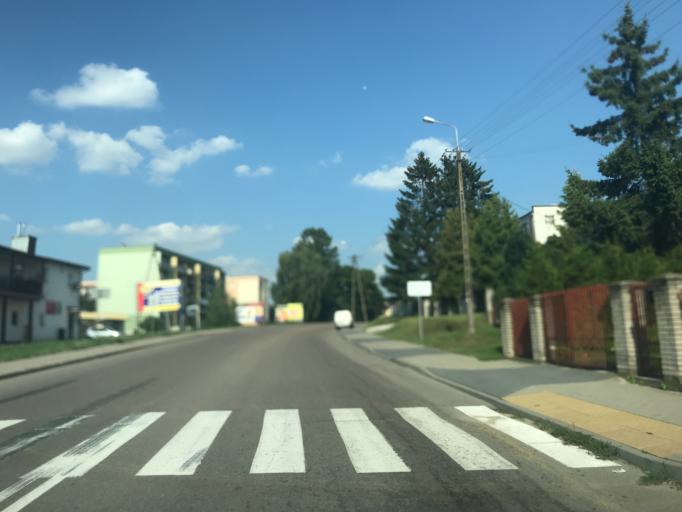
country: PL
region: Masovian Voivodeship
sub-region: Powiat mlawski
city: Mlawa
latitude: 53.1078
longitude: 20.3684
